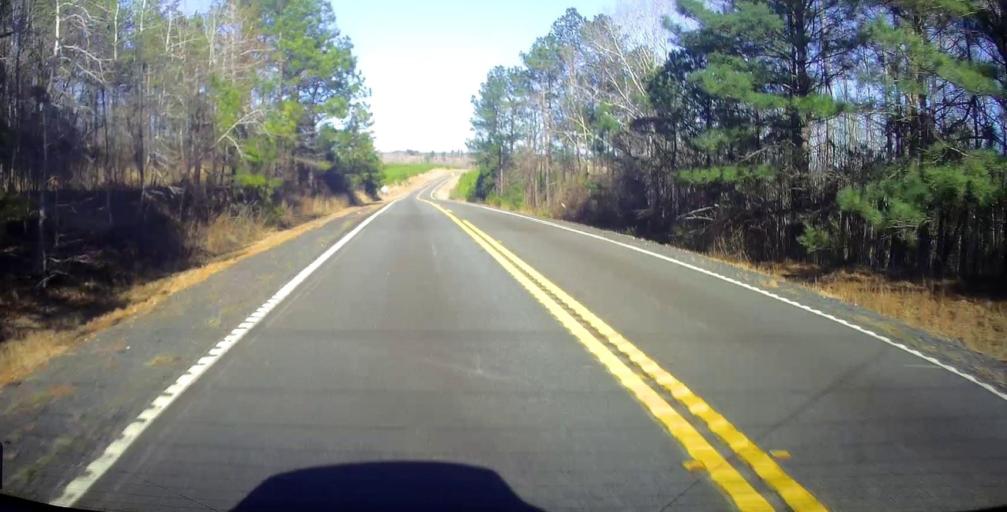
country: US
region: Georgia
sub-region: Talbot County
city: Talbotton
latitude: 32.6472
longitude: -84.4127
